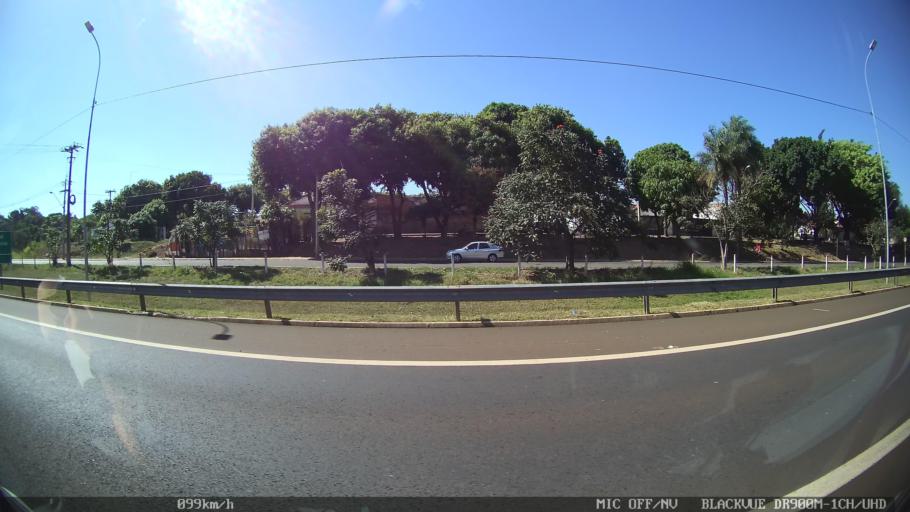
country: BR
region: Sao Paulo
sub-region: Franca
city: Franca
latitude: -20.4873
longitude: -47.4087
